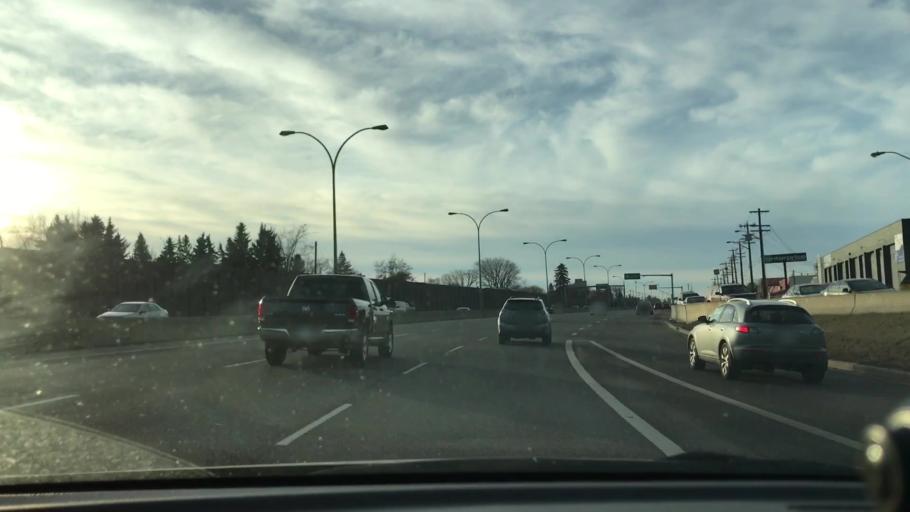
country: CA
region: Alberta
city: Edmonton
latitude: 53.5815
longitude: -113.4719
